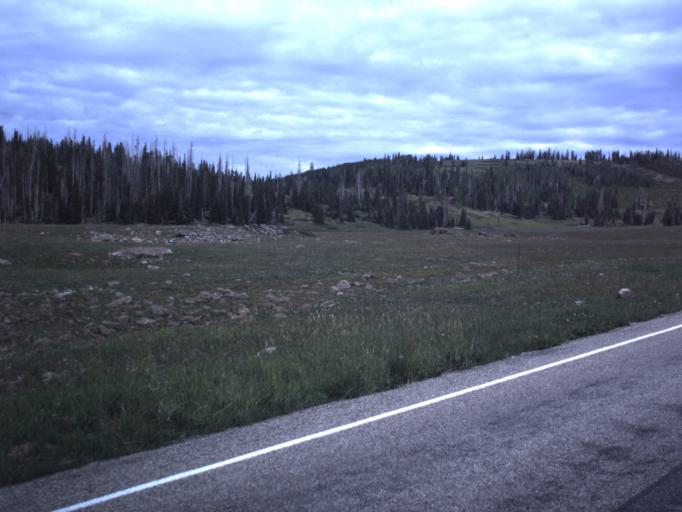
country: US
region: Utah
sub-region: Iron County
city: Cedar City
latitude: 37.5916
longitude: -112.8491
